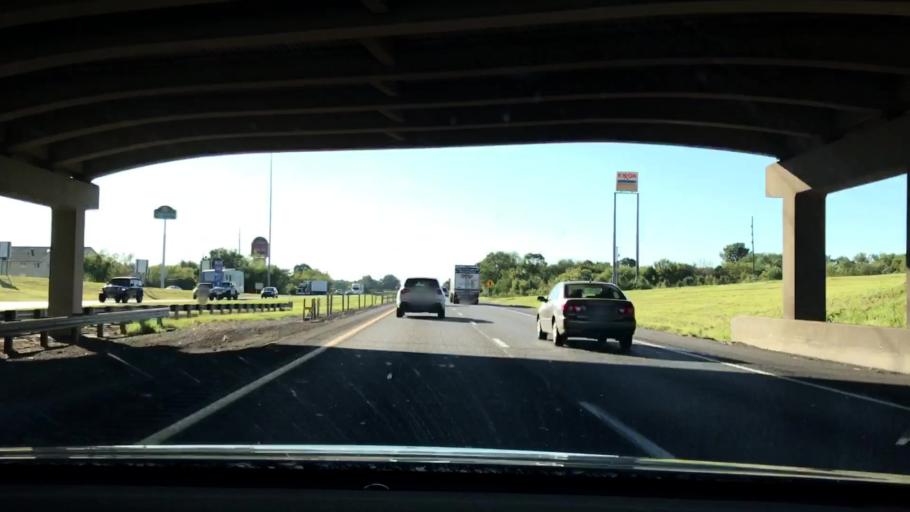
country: US
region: Tennessee
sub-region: Wilson County
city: Lebanon
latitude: 36.1828
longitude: -86.2993
